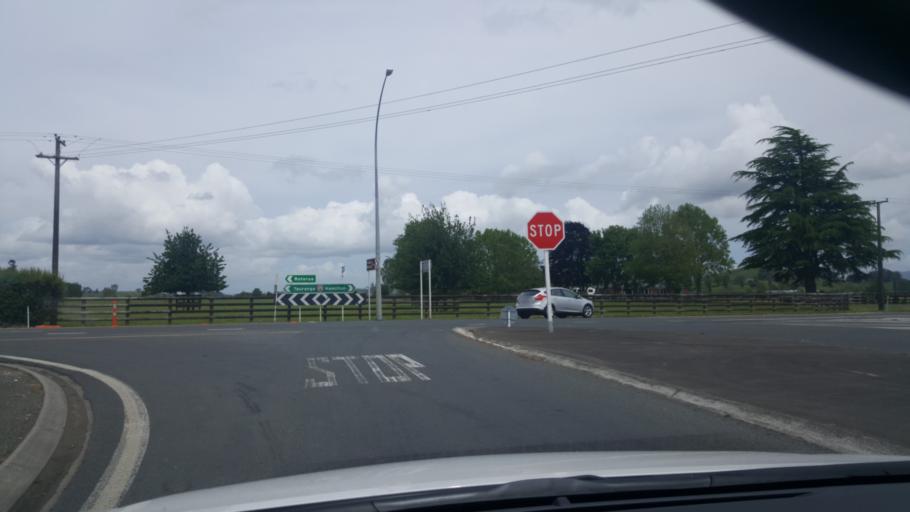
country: NZ
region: Waikato
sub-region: Matamata-Piako District
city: Matamata
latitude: -37.8831
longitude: 175.7329
